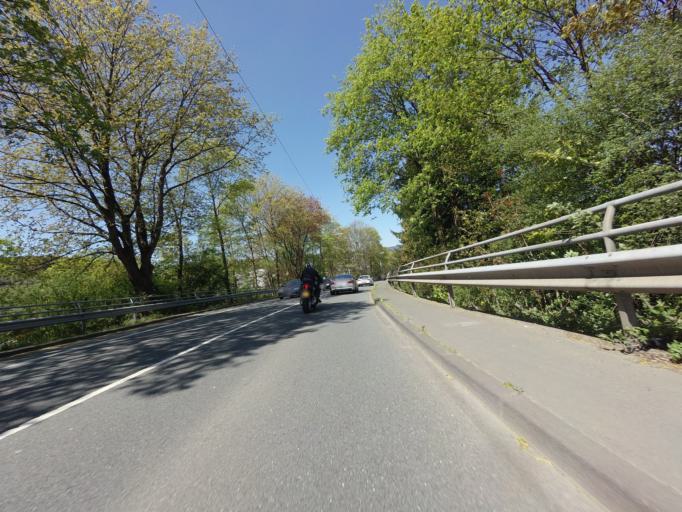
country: DE
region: North Rhine-Westphalia
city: Kreuztal
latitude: 50.9723
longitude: 7.9789
